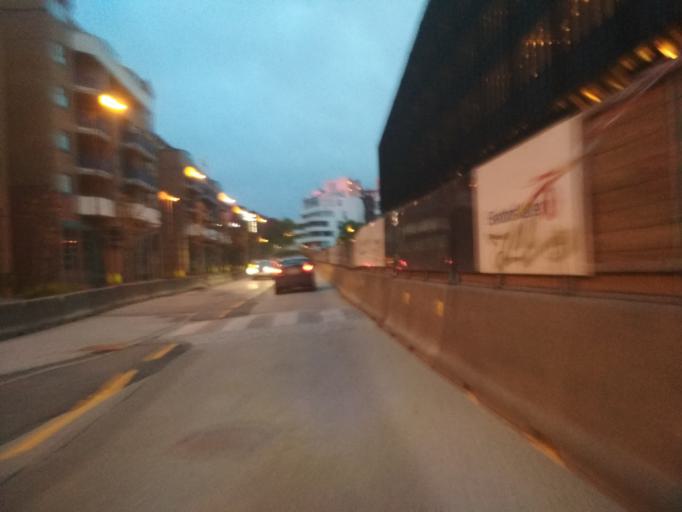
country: NO
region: Rogaland
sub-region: Stavanger
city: Stavanger
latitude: 58.9751
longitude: 5.7197
